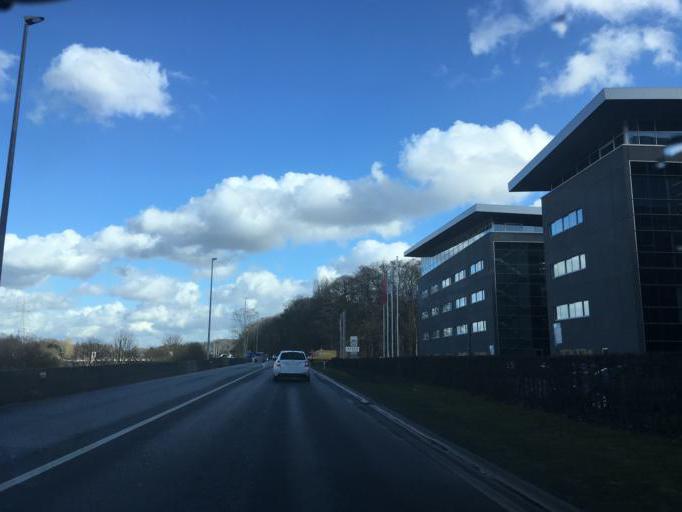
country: BE
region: Flanders
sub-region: Provincie Oost-Vlaanderen
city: Merelbeke
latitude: 51.0059
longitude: 3.7538
